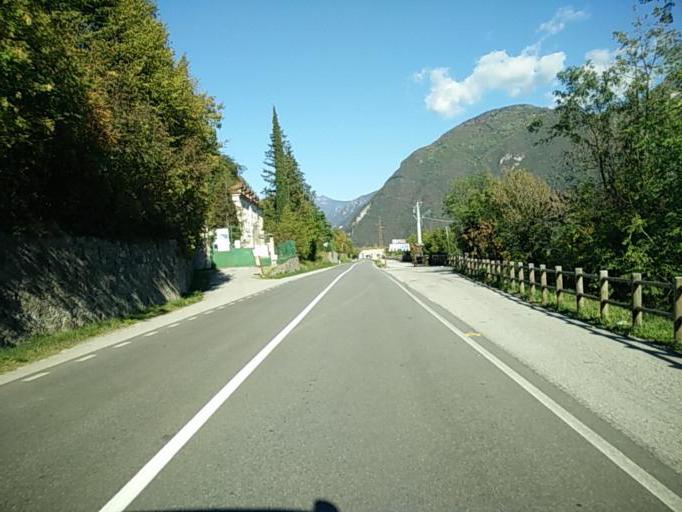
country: IT
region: Lombardy
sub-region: Provincia di Brescia
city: Anfo
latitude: 45.7714
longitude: 10.4994
